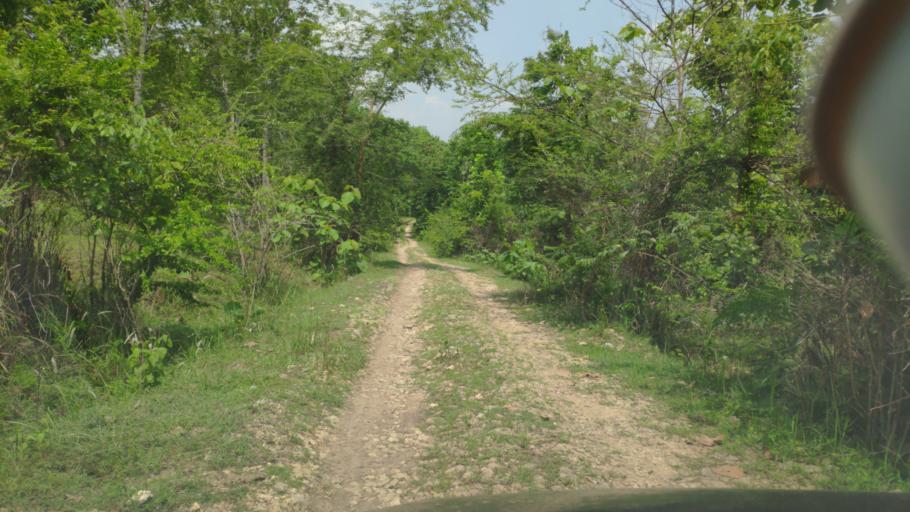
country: ID
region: Central Java
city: Sumberejo
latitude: -6.9287
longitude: 111.3058
